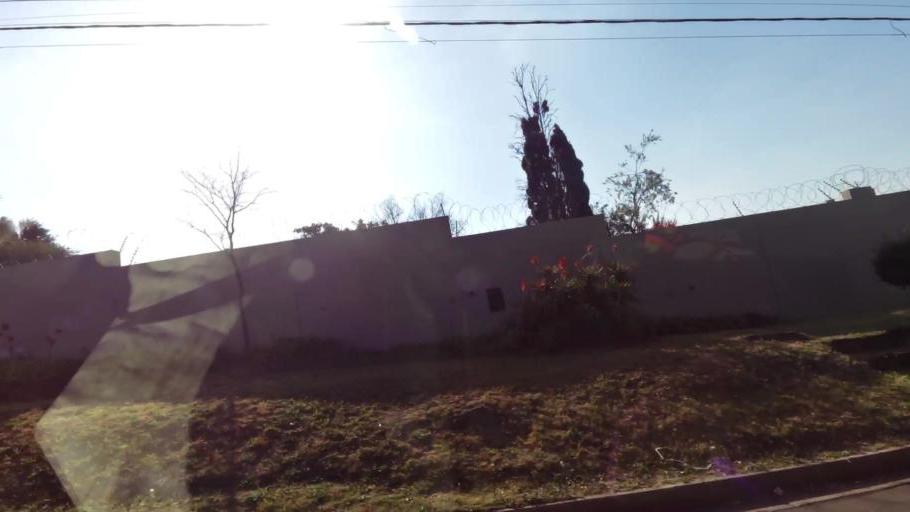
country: ZA
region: Gauteng
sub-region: City of Johannesburg Metropolitan Municipality
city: Johannesburg
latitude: -26.1772
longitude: 27.9980
